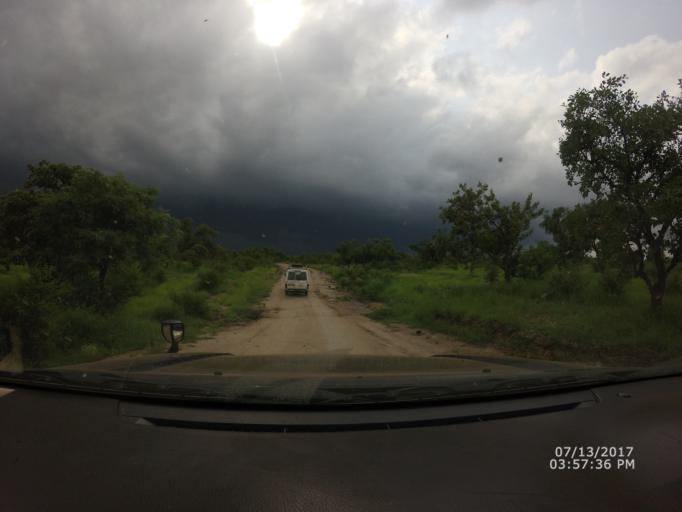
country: UG
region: Northern Region
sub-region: Yumbe District
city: Yumbe
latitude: 3.2955
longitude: 31.3017
